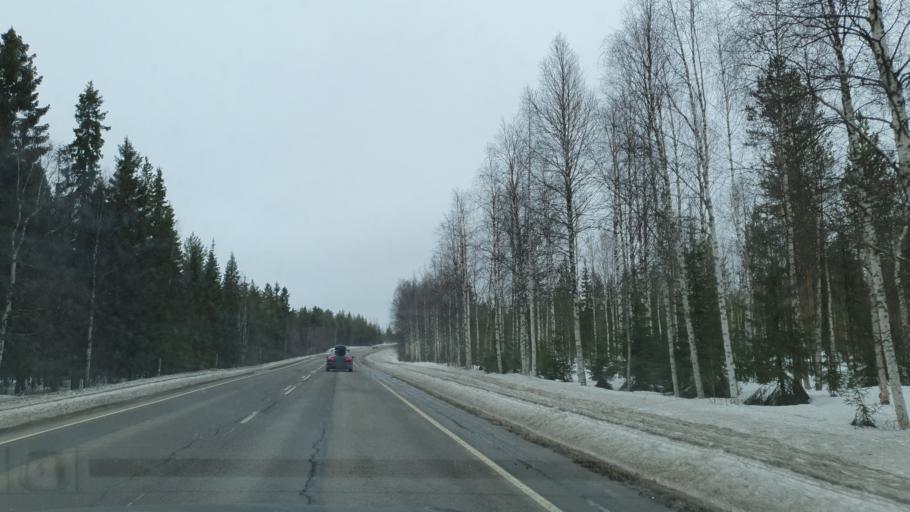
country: FI
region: Lapland
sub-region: Torniolaakso
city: Pello
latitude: 66.8385
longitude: 24.0112
